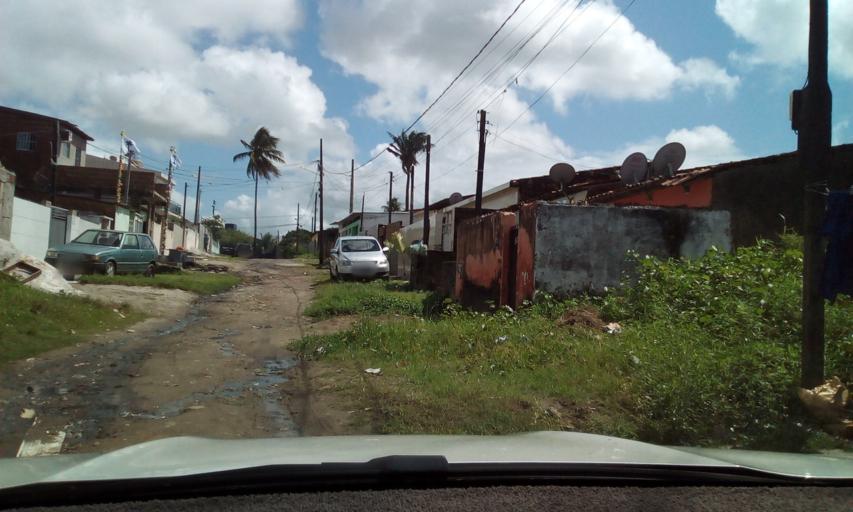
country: BR
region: Paraiba
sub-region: Bayeux
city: Bayeux
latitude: -7.1291
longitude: -34.9257
